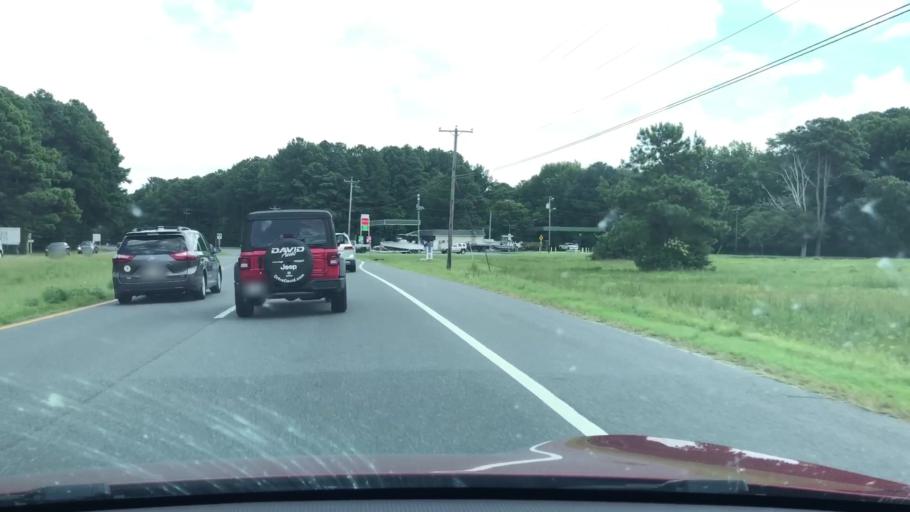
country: US
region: Virginia
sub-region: Northampton County
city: Exmore
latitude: 37.5408
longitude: -75.8177
